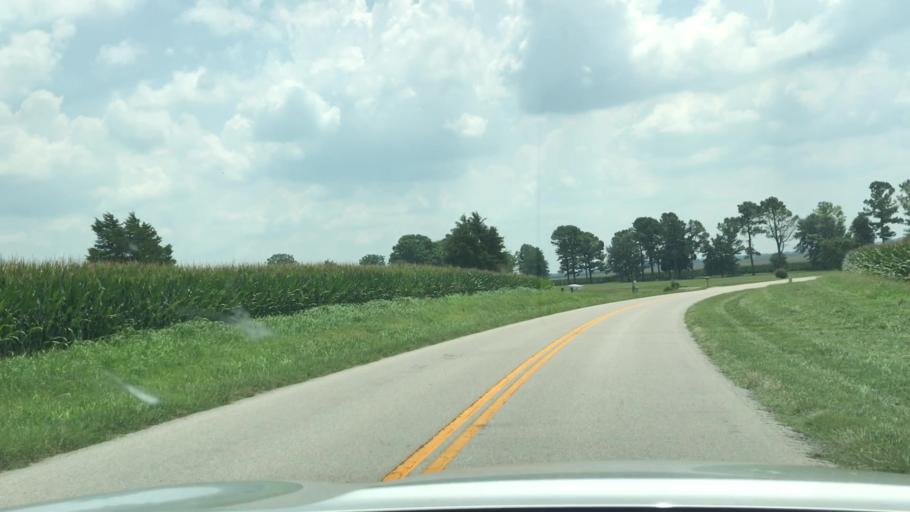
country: US
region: Kentucky
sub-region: Todd County
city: Elkton
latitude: 36.7584
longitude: -87.0966
